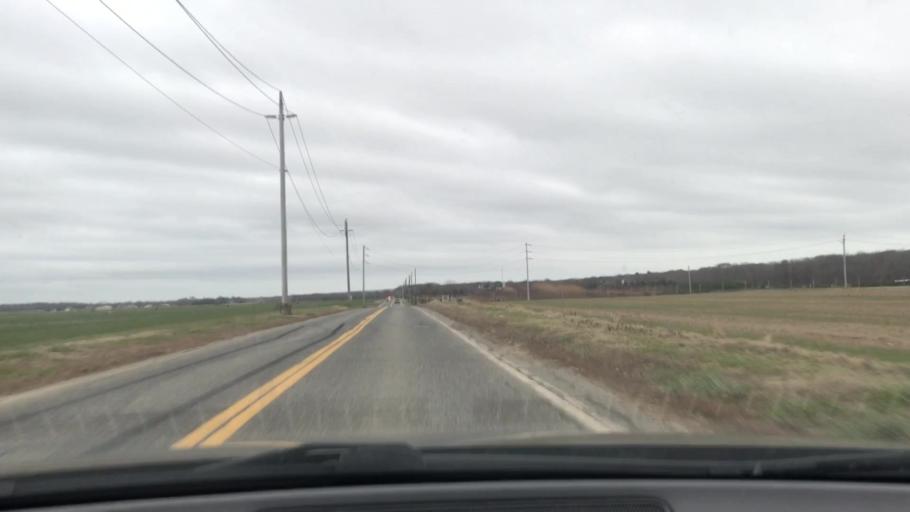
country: US
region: New York
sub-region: Suffolk County
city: Riverhead
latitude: 40.9622
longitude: -72.6709
